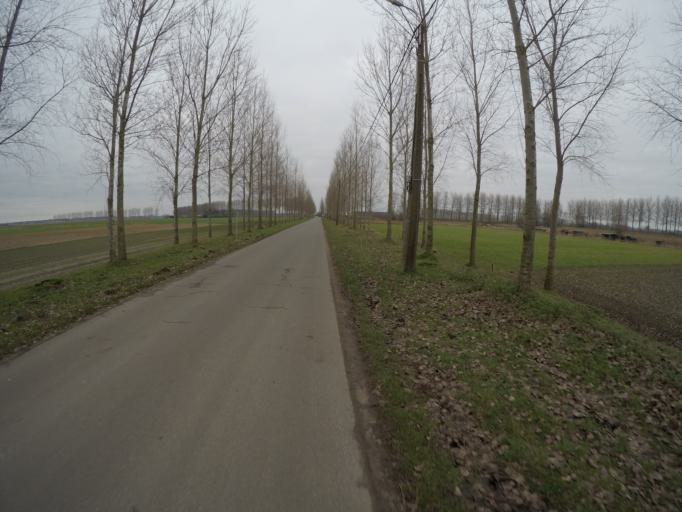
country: BE
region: Flanders
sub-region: Provincie Oost-Vlaanderen
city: Sint-Gillis-Waas
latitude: 51.2423
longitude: 4.1262
